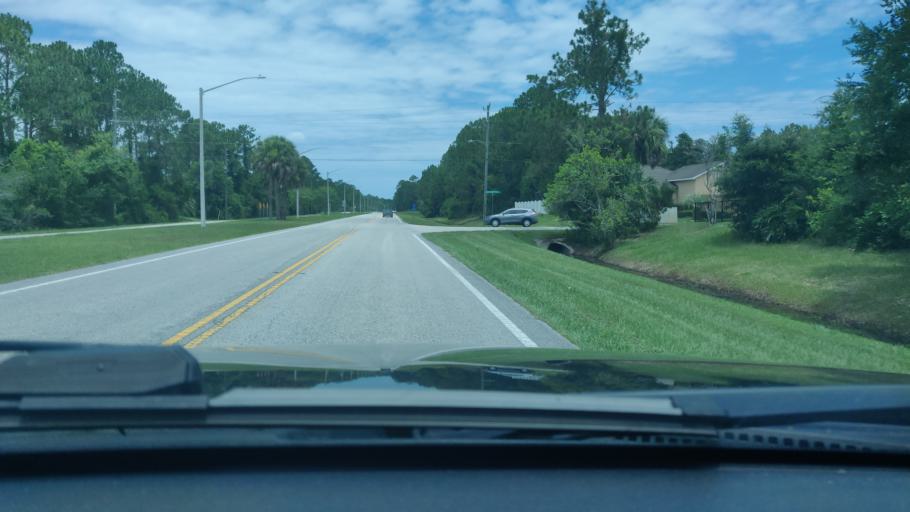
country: US
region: Florida
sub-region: Flagler County
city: Palm Coast
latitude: 29.5384
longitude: -81.2547
